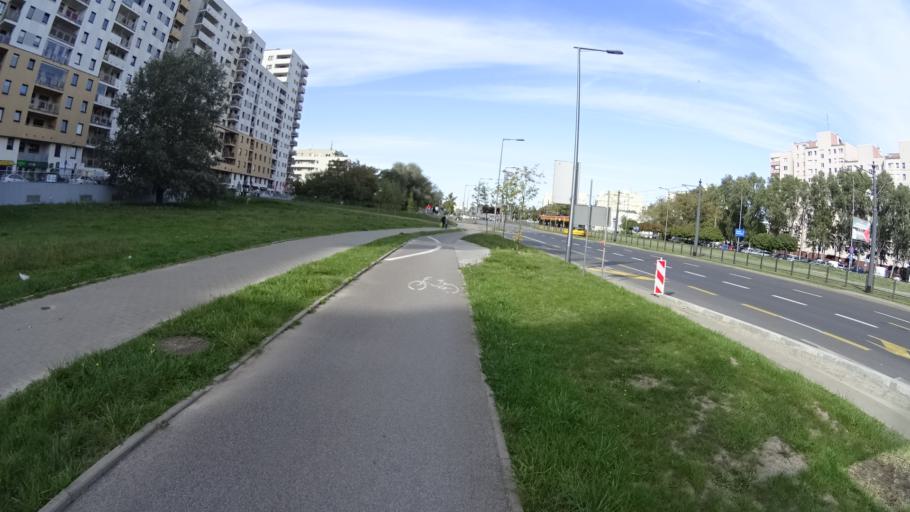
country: PL
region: Masovian Voivodeship
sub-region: Warszawa
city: Bemowo
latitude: 52.2404
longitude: 20.9125
